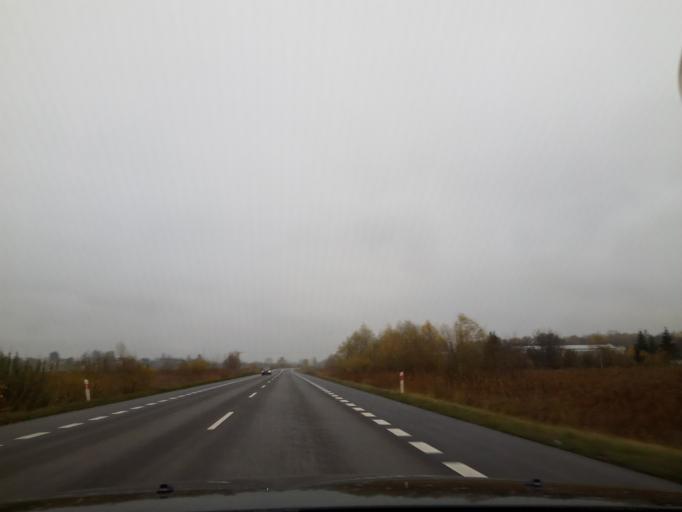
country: PL
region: Lesser Poland Voivodeship
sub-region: Powiat proszowicki
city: Proszowice
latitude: 50.1979
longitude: 20.2824
